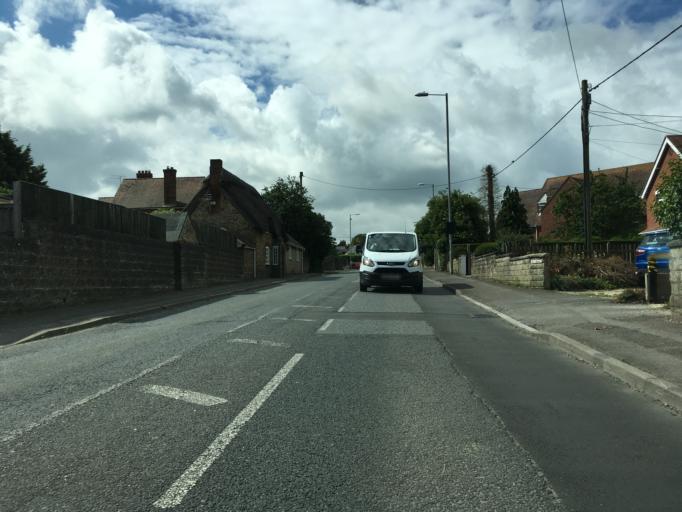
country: GB
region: England
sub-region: Borough of Swindon
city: Highworth
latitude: 51.6356
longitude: -1.7097
